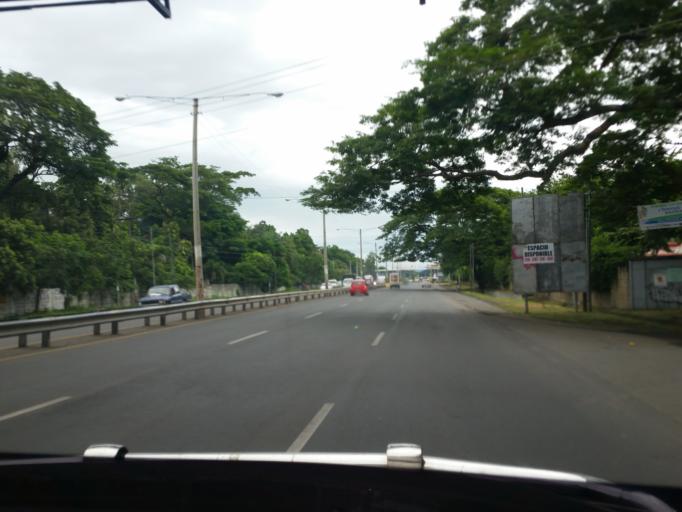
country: NI
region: Managua
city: Tipitapa
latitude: 12.1470
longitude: -86.1620
